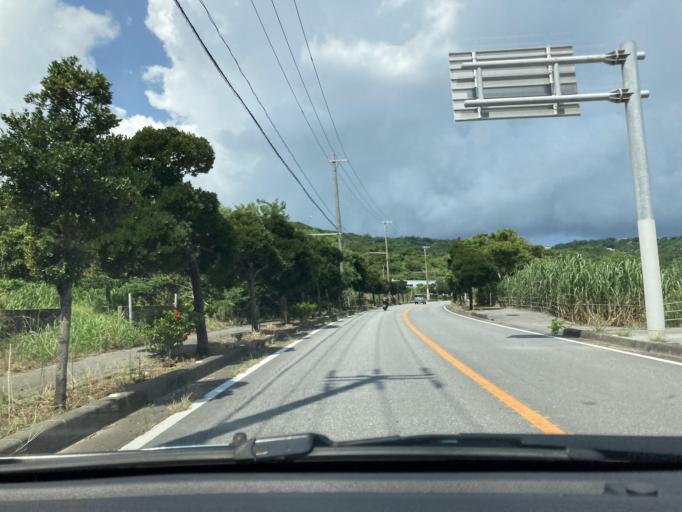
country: JP
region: Okinawa
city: Tomigusuku
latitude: 26.1726
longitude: 127.7699
